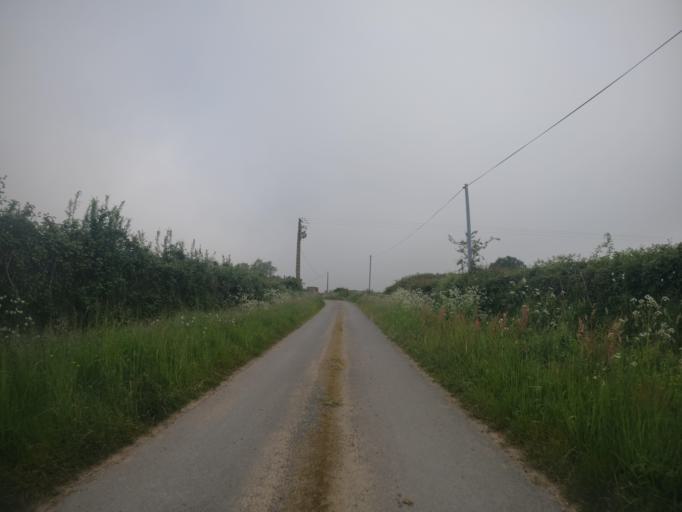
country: FR
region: Poitou-Charentes
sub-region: Departement des Deux-Sevres
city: Chiche
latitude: 46.8952
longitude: -0.3442
